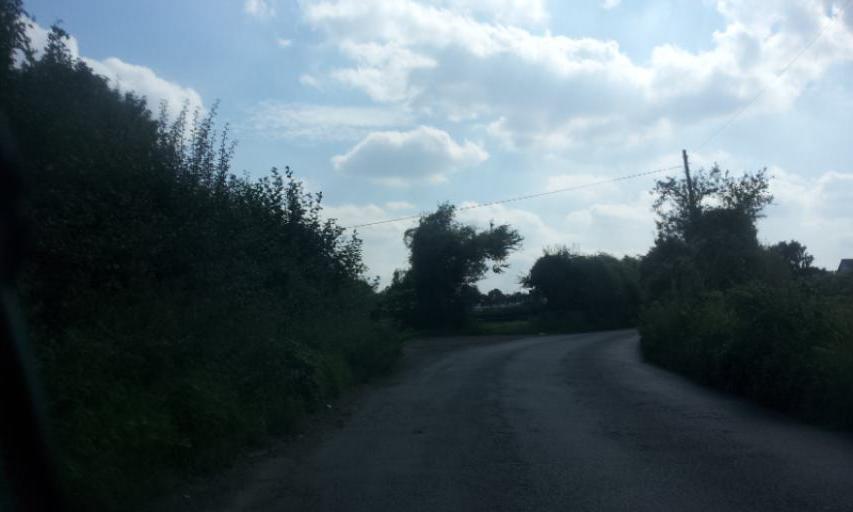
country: GB
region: England
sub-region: Kent
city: Maidstone
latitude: 51.2504
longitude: 0.5129
